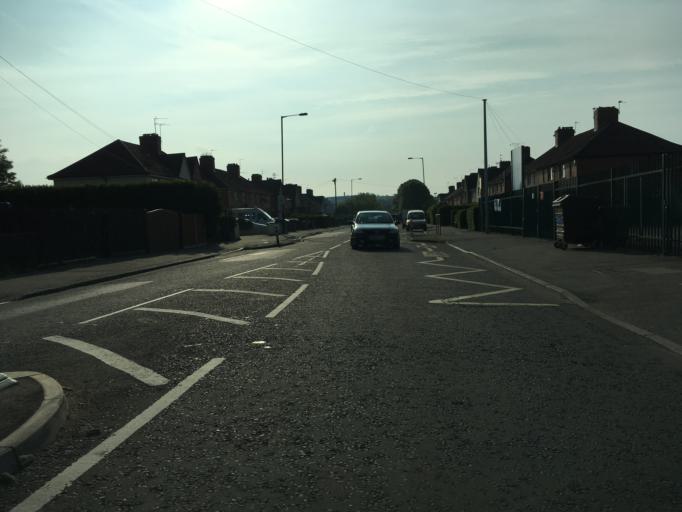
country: GB
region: England
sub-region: Bristol
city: Bristol
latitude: 51.5000
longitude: -2.6065
